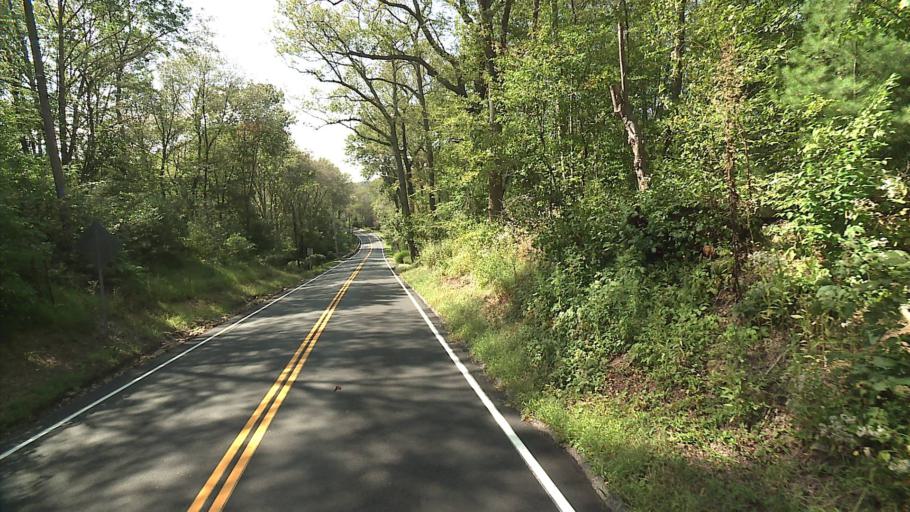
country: US
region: Connecticut
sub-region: Tolland County
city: Hebron
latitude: 41.7225
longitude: -72.4131
